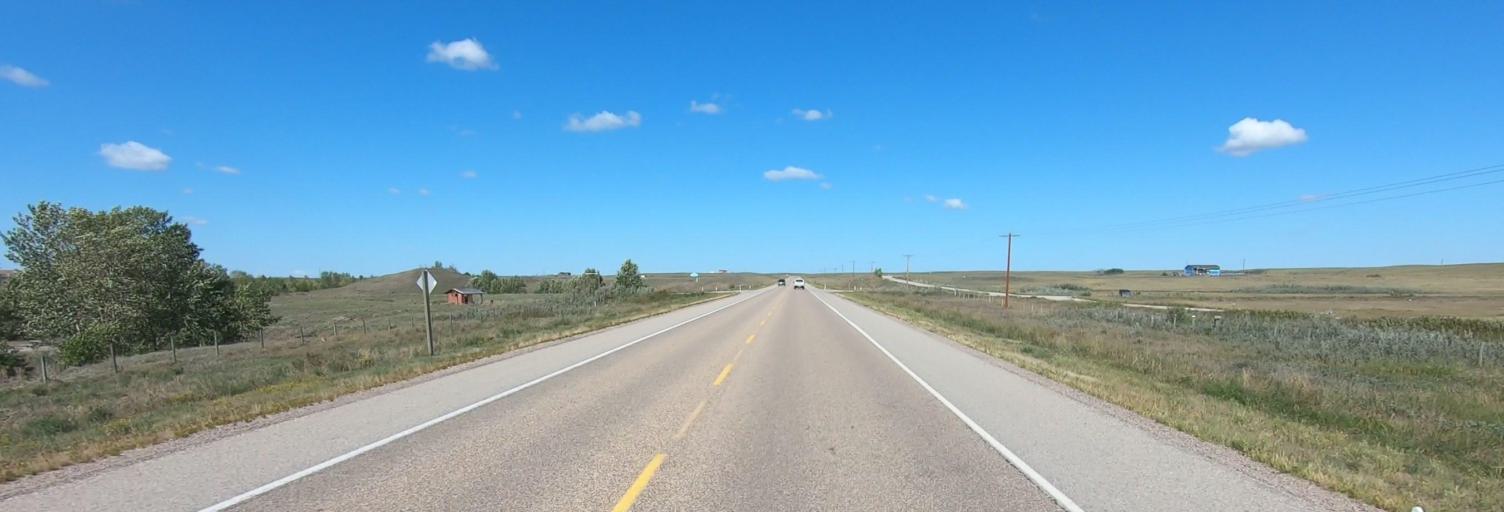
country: CA
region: Alberta
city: Strathmore
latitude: 50.8590
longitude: -113.1375
